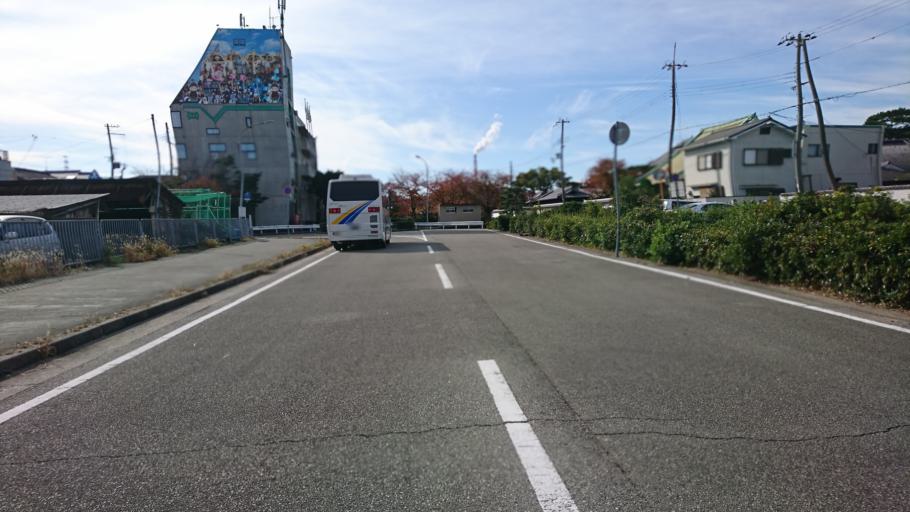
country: JP
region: Hyogo
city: Kakogawacho-honmachi
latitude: 34.7482
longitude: 134.8009
